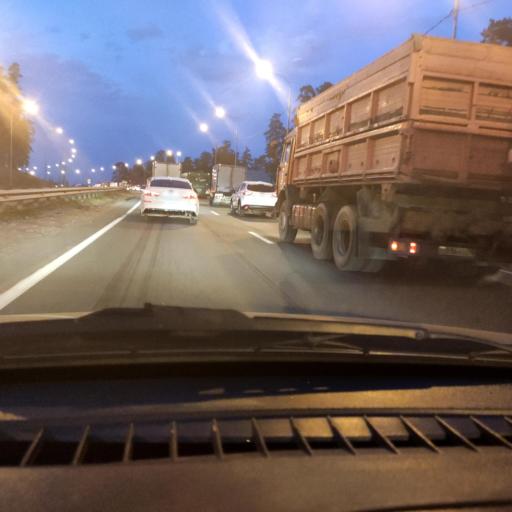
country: RU
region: Samara
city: Zhigulevsk
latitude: 53.5365
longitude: 49.5166
